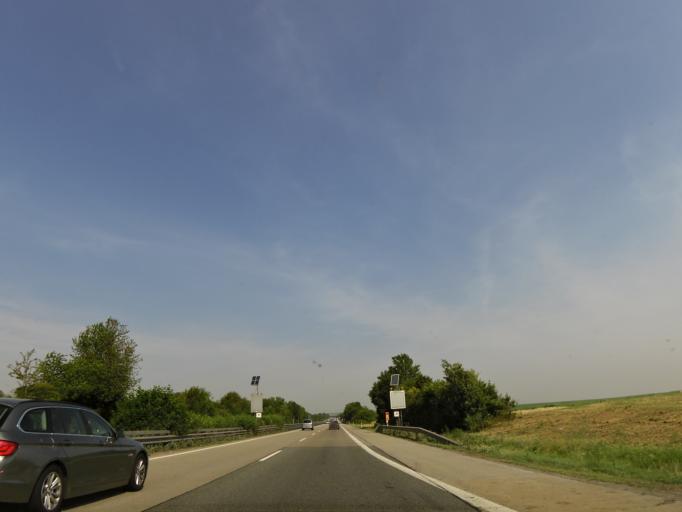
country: DE
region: Rheinland-Pfalz
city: Morstadt
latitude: 49.6700
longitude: 8.2671
